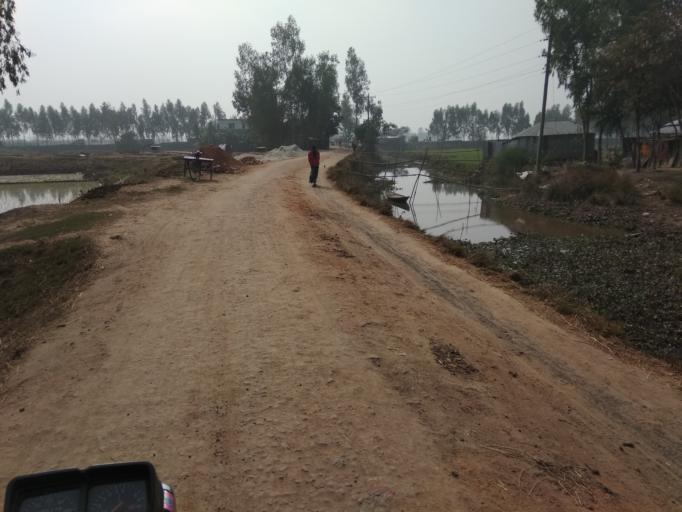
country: BD
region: Rajshahi
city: Bogra
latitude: 24.4784
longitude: 89.2673
